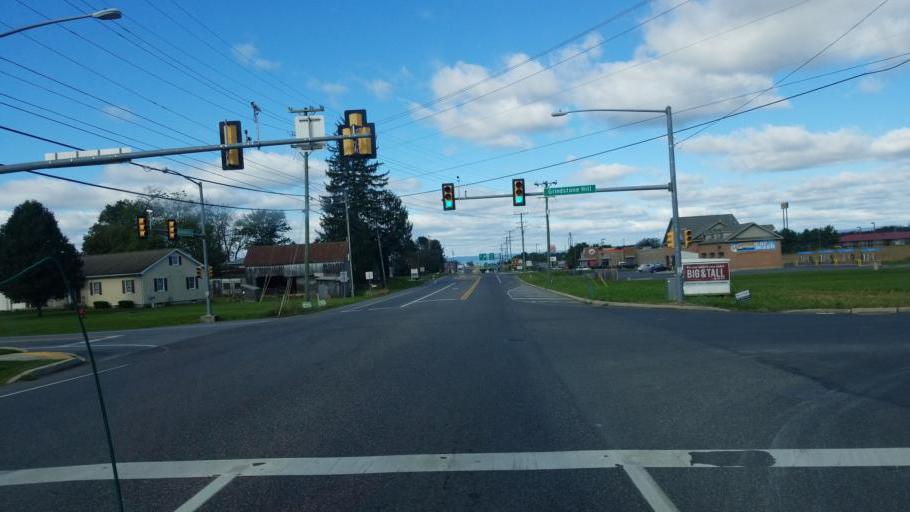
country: US
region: Pennsylvania
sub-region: Franklin County
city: Greencastle
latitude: 39.7853
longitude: -77.7065
